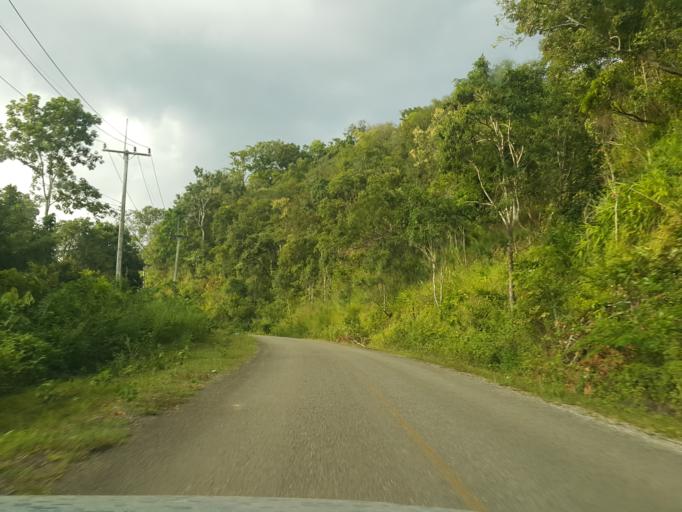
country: TH
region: Mae Hong Son
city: Khun Yuam
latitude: 18.7512
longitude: 98.1941
